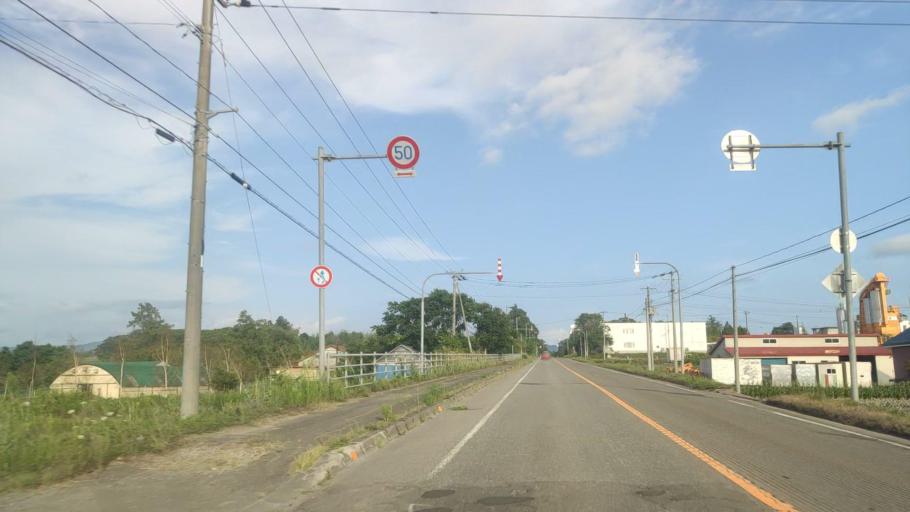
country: JP
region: Hokkaido
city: Iwamizawa
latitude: 43.0258
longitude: 141.8414
